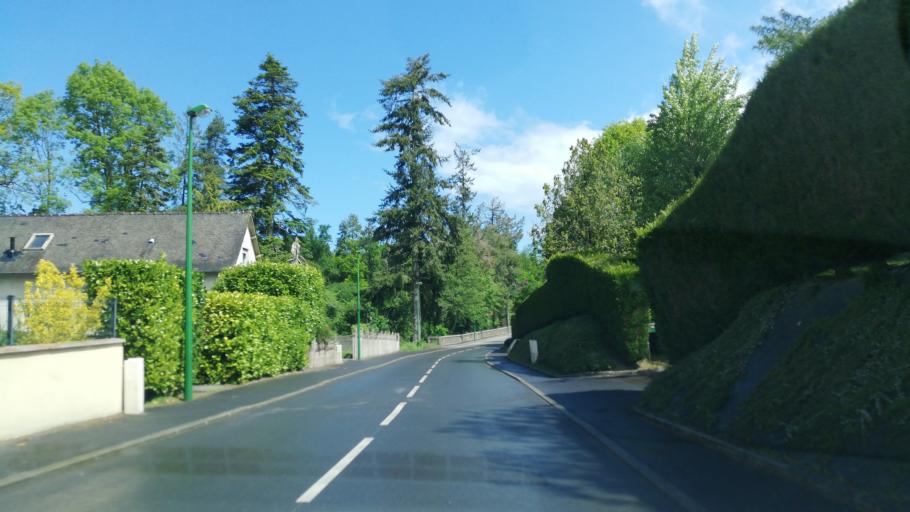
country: FR
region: Brittany
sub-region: Departement d'Ille-et-Vilaine
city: Irodouer
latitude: 48.2519
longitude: -1.9491
